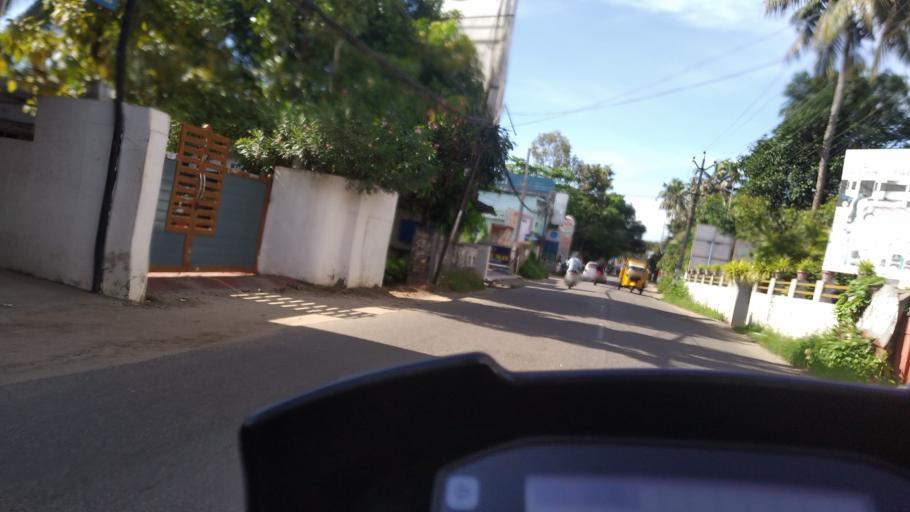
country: IN
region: Kerala
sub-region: Ernakulam
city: Elur
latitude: 10.0575
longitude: 76.2148
